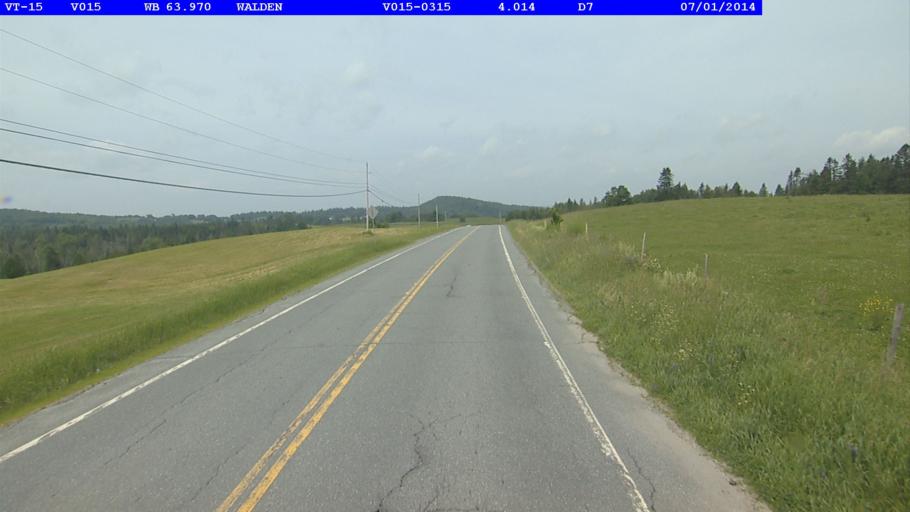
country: US
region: Vermont
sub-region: Caledonia County
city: Hardwick
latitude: 44.4487
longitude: -72.2470
